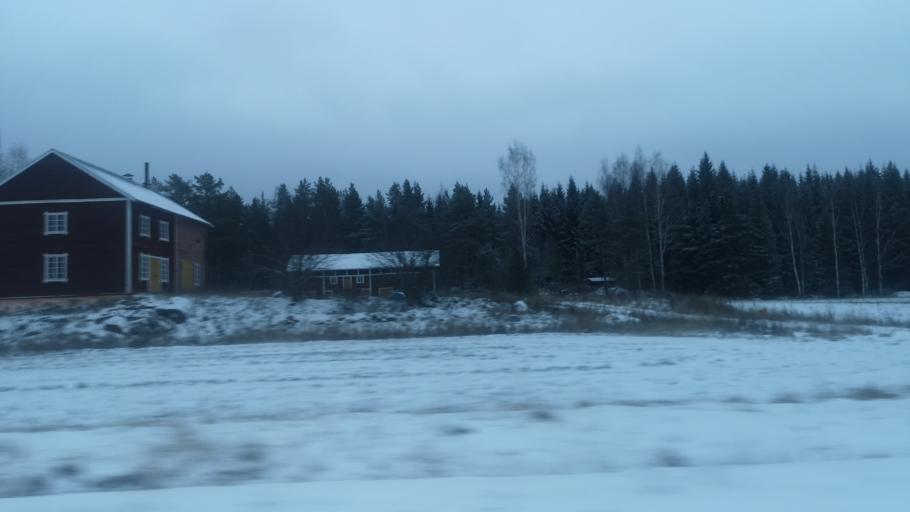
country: FI
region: Southern Savonia
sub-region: Savonlinna
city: Enonkoski
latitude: 62.0893
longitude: 28.6789
